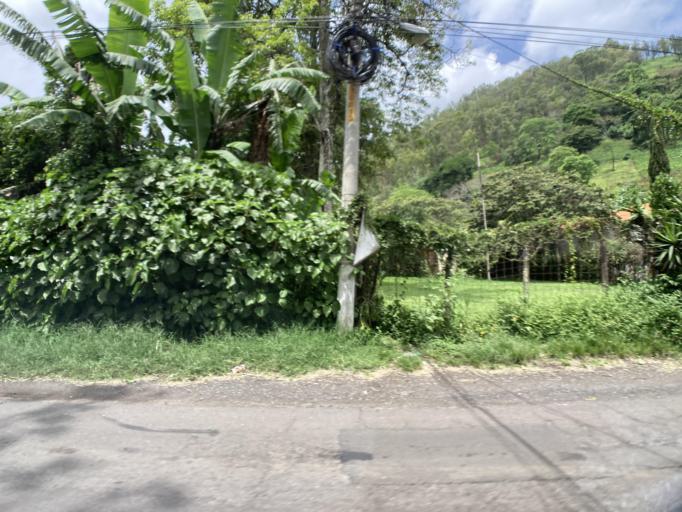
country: GT
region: Guatemala
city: Villa Canales
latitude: 14.4286
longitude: -90.5568
